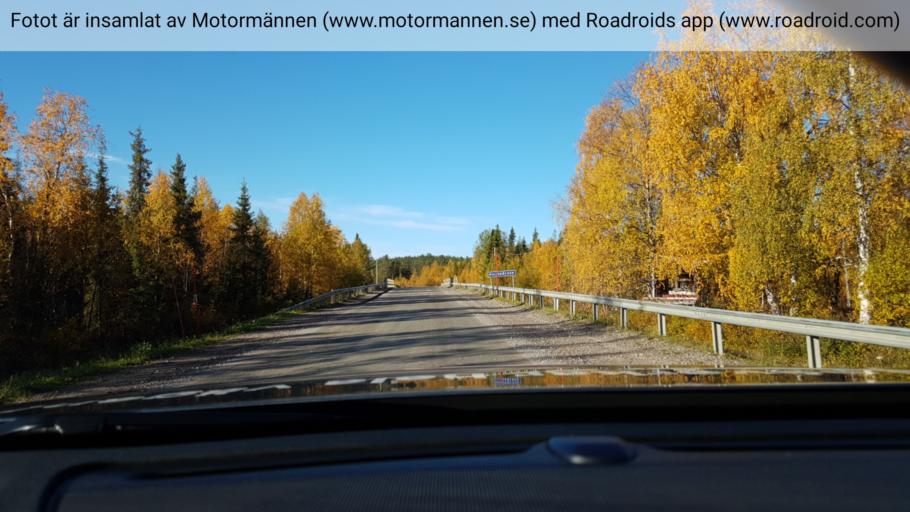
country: SE
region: Norrbotten
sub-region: Alvsbyns Kommun
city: AElvsbyn
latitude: 66.2783
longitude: 21.1031
